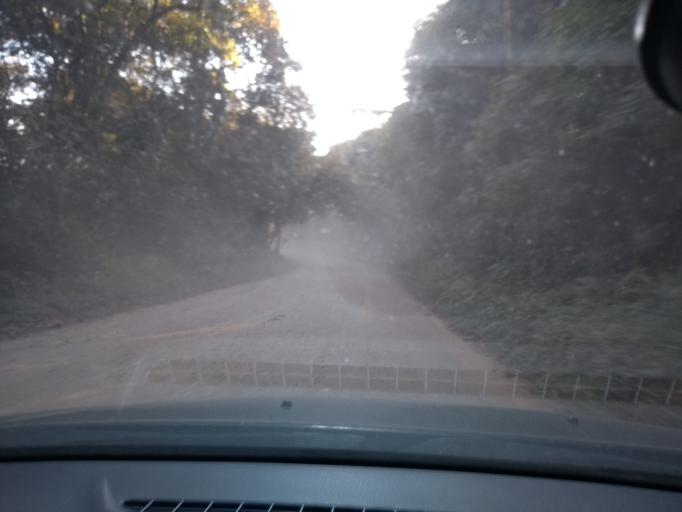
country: BR
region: Sao Paulo
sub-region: Sao Bernardo Do Campo
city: Sao Bernardo do Campo
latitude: -23.7758
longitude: -46.5045
